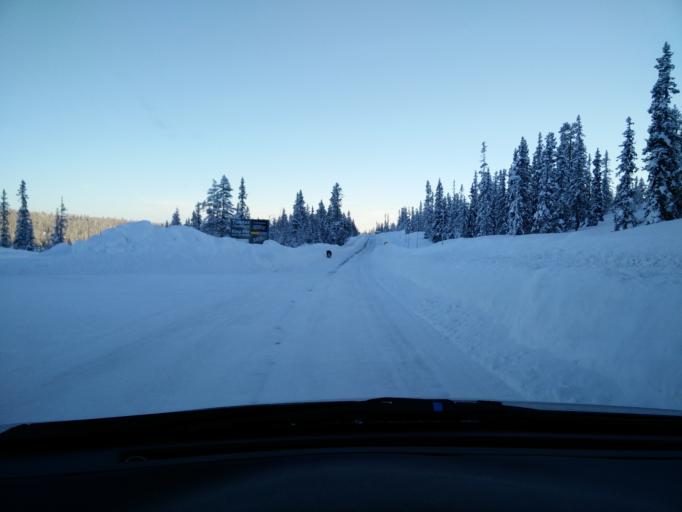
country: SE
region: Jaemtland
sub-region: Bergs Kommun
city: Hoverberg
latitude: 62.5000
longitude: 14.1094
